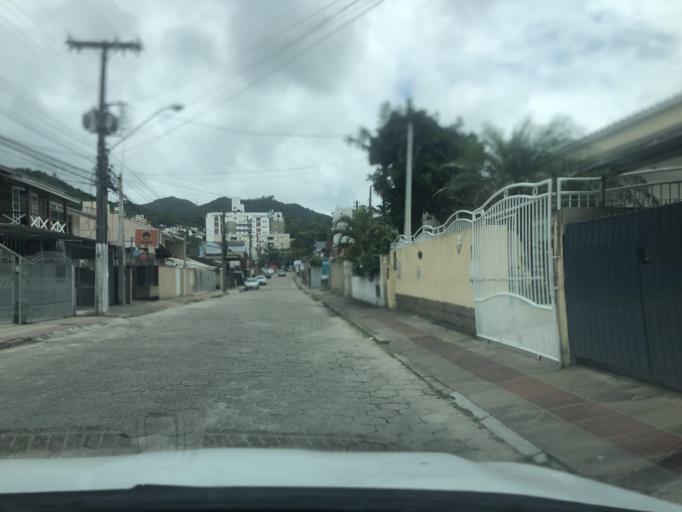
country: BR
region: Santa Catarina
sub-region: Florianopolis
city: Corrego Grande
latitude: -27.5986
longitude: -48.5131
